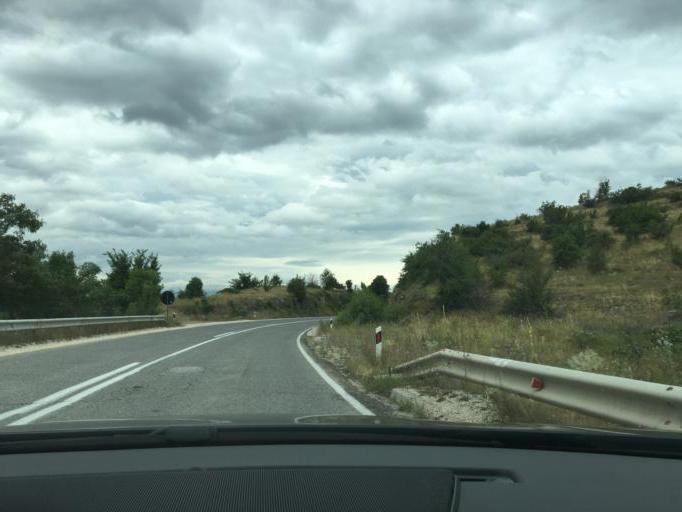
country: MK
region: Opstina Rankovce
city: Rankovce
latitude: 42.1461
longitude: 22.0051
